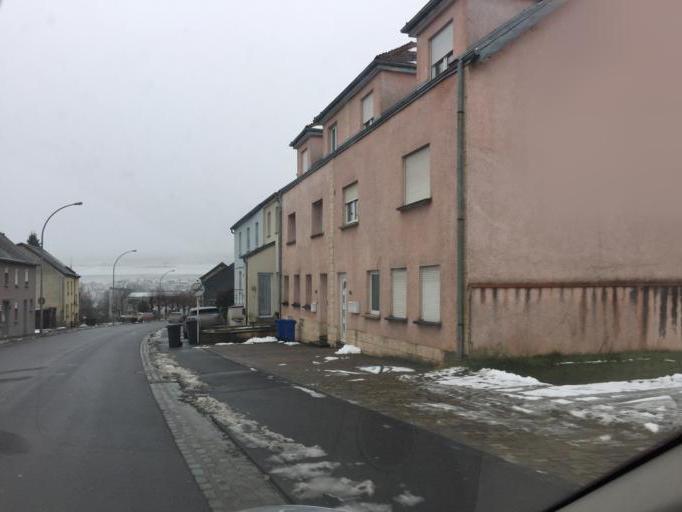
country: LU
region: Diekirch
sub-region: Canton de Diekirch
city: Niederfeulen
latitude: 49.8567
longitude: 6.0408
